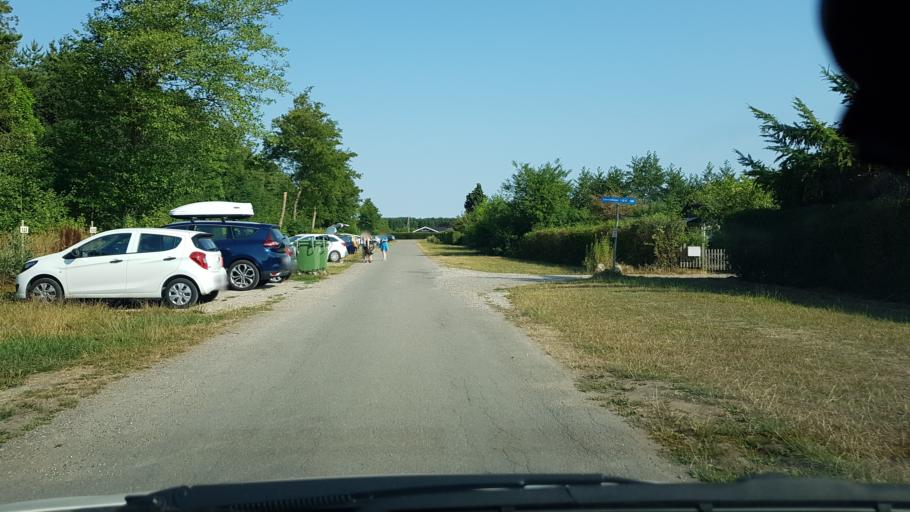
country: DK
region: Capital Region
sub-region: Vallensbaek Kommune
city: Vallensbaek
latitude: 55.6337
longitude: 12.3889
